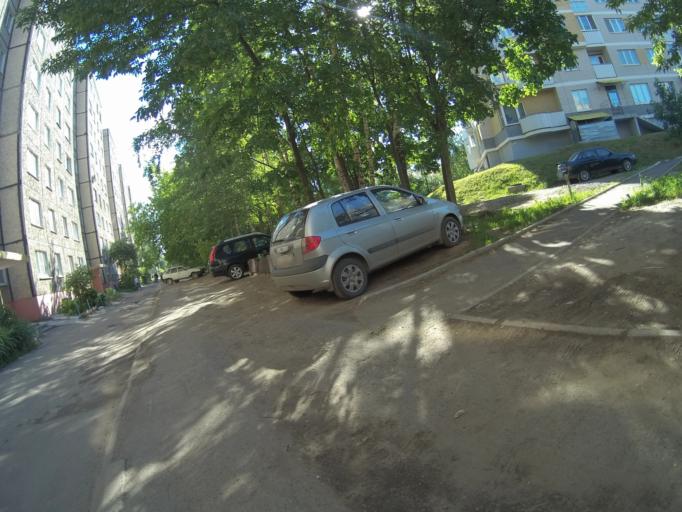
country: RU
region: Vladimir
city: Kommunar
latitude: 56.1617
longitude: 40.4692
